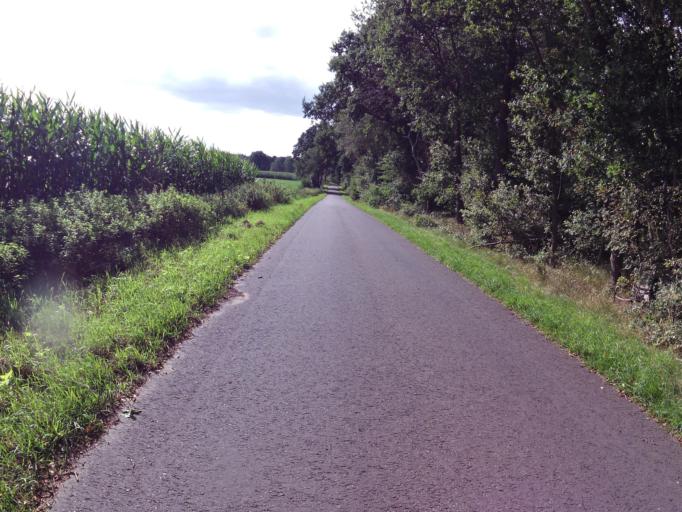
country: DE
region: Lower Saxony
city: Sandbostel
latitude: 53.4426
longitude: 9.1245
